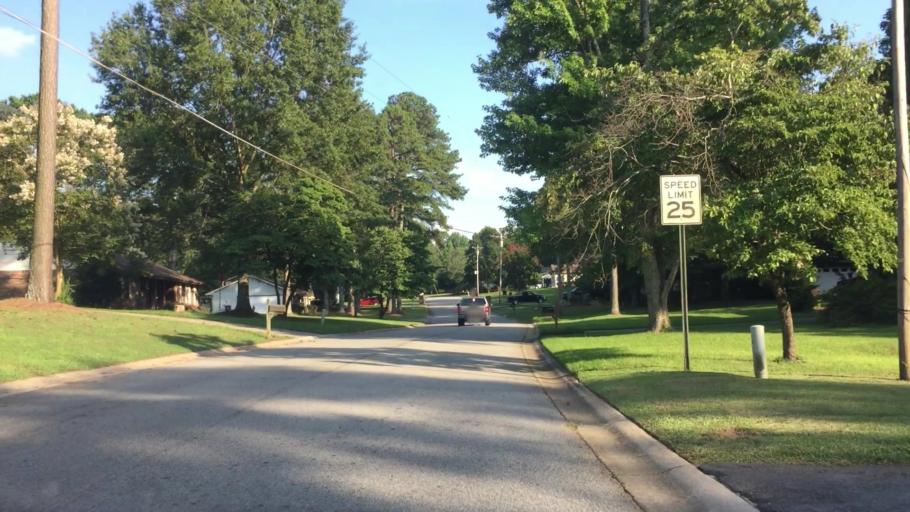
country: US
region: Georgia
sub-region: Henry County
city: Stockbridge
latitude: 33.6229
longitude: -84.2321
